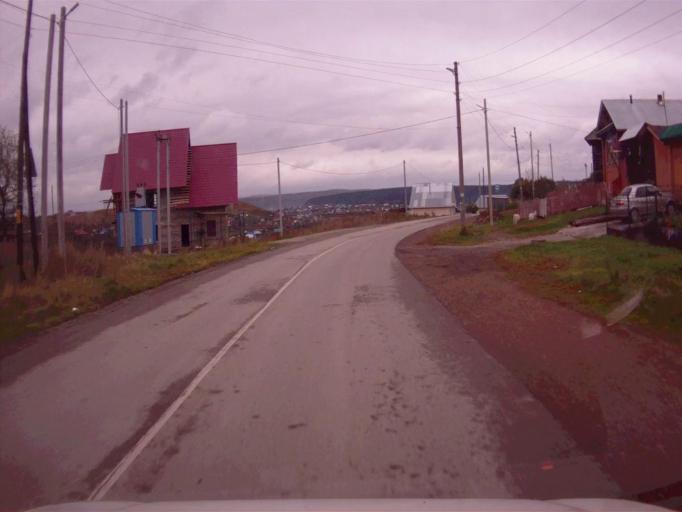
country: RU
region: Chelyabinsk
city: Nyazepetrovsk
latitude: 56.0619
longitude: 59.6167
